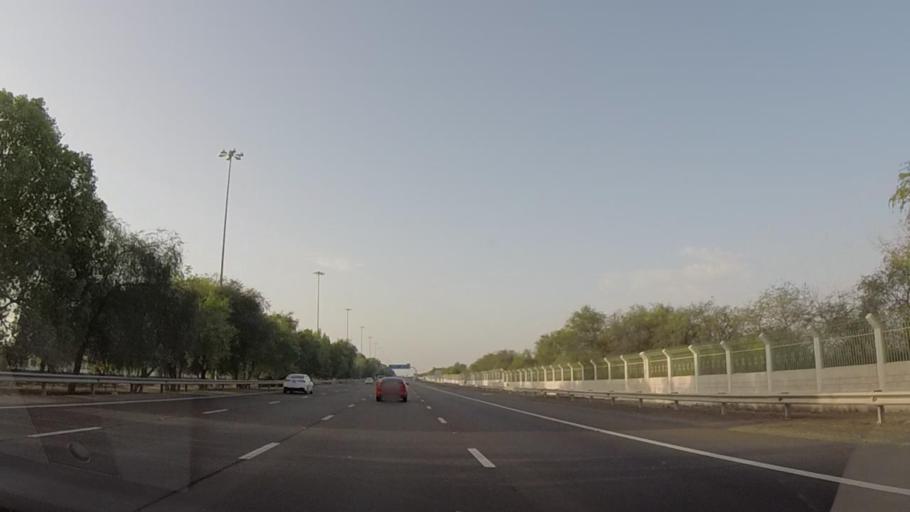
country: AE
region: Dubai
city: Dubai
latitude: 24.8092
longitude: 54.8684
